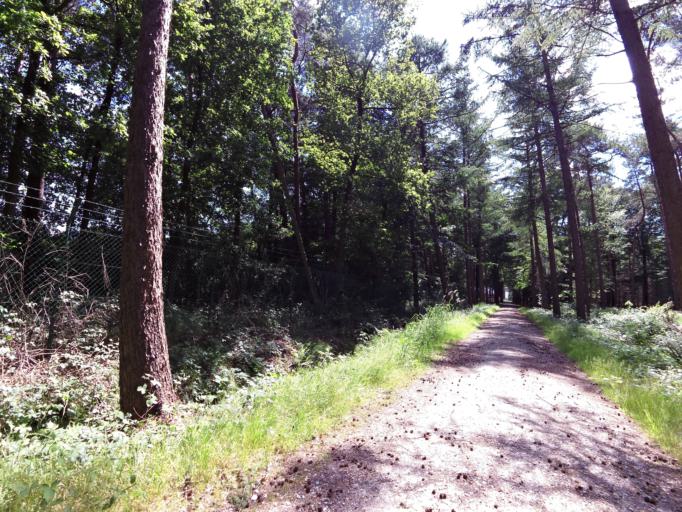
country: BE
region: Flanders
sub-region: Provincie West-Vlaanderen
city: Zedelgem
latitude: 51.1442
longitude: 3.1118
